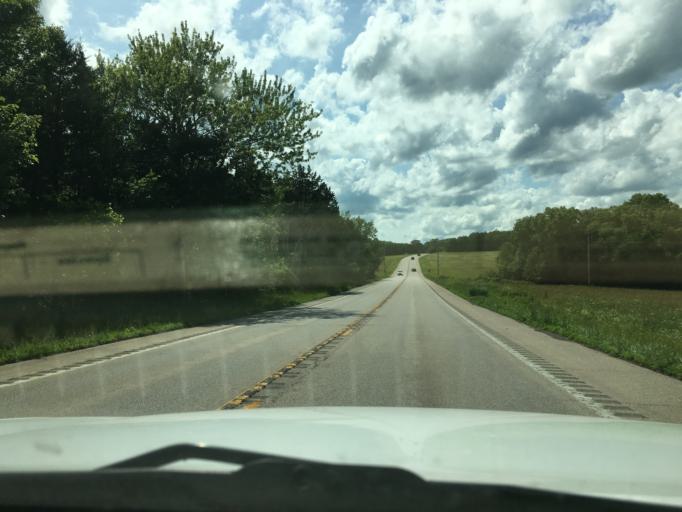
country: US
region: Missouri
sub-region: Franklin County
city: Gerald
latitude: 38.4196
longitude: -91.2513
